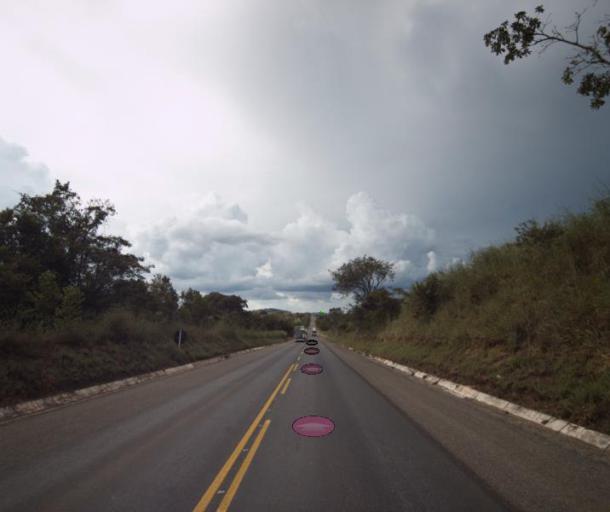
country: BR
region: Goias
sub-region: Ceres
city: Ceres
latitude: -15.1861
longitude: -49.5450
